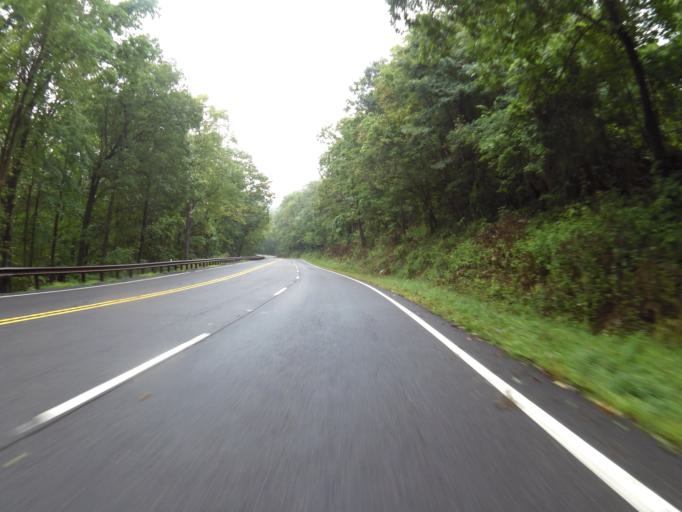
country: US
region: Virginia
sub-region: Rappahannock County
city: Washington
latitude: 38.6615
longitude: -78.3036
